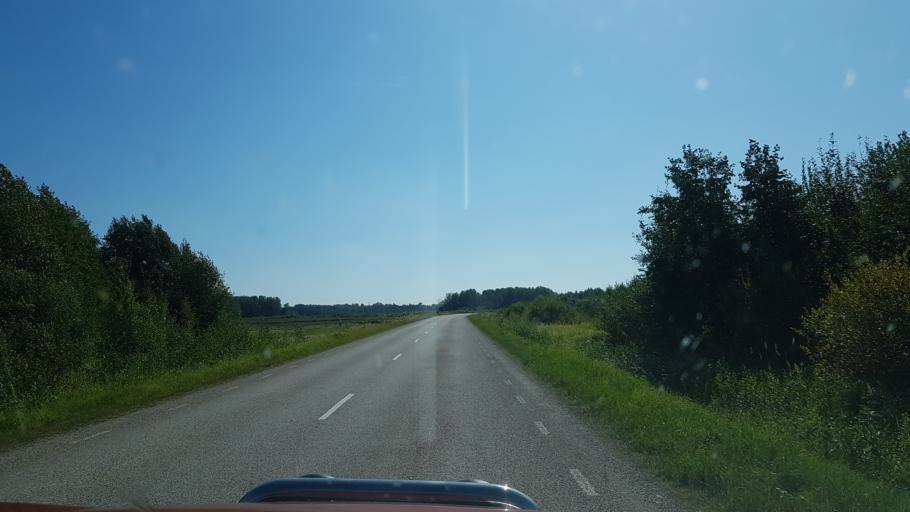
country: EE
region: Polvamaa
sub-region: Polva linn
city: Polva
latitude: 58.2369
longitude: 27.2147
